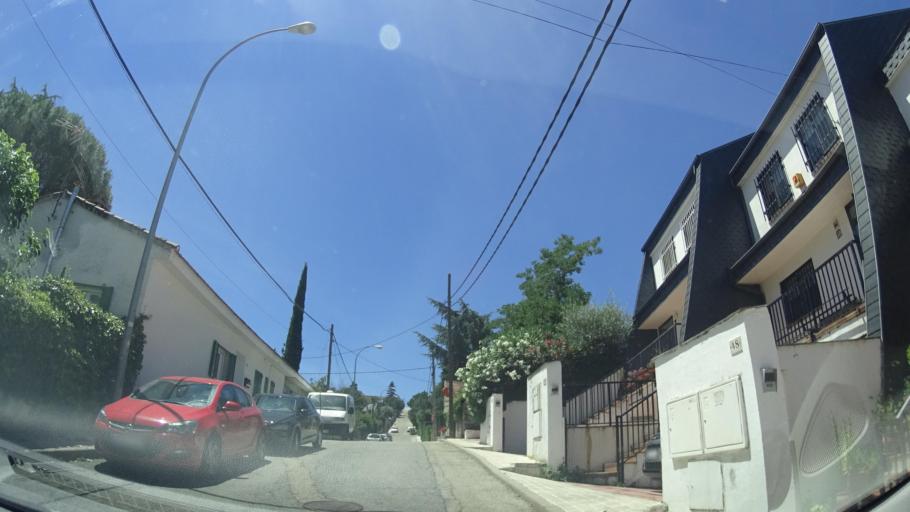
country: ES
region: Madrid
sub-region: Provincia de Madrid
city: Galapagar
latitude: 40.5952
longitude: -3.9873
